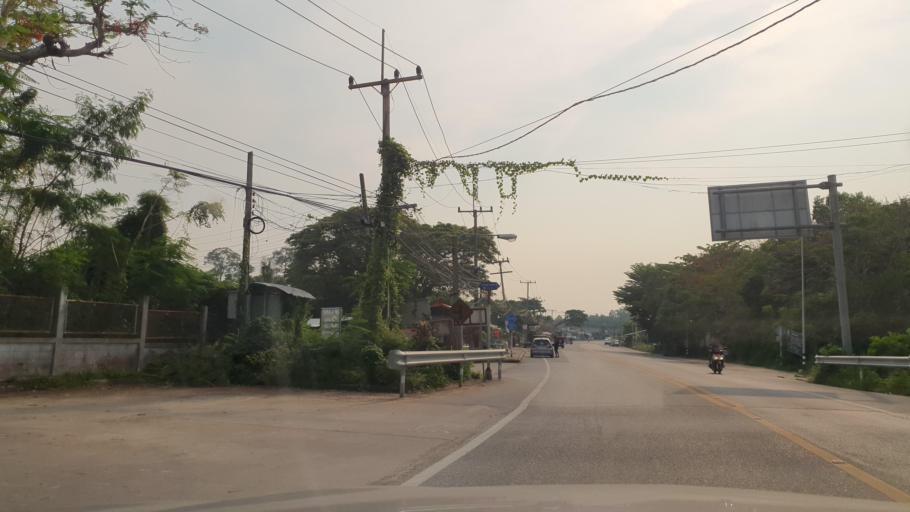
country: TH
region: Rayong
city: Rayong
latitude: 12.6159
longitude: 101.4205
